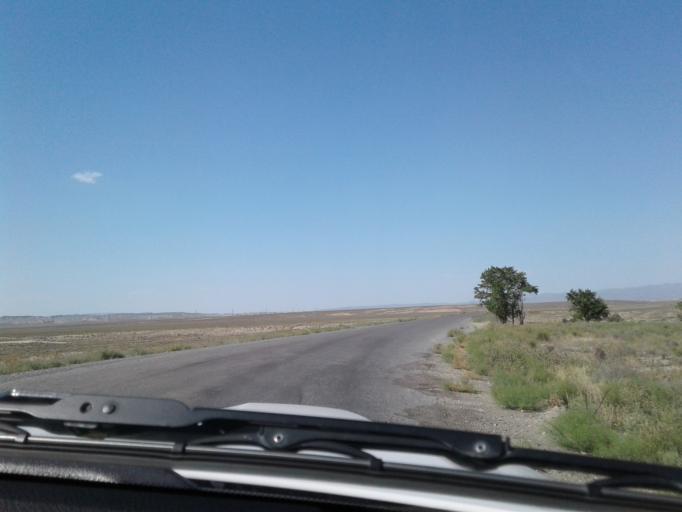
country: TM
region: Balkan
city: Magtymguly
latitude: 38.5997
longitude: 56.1946
